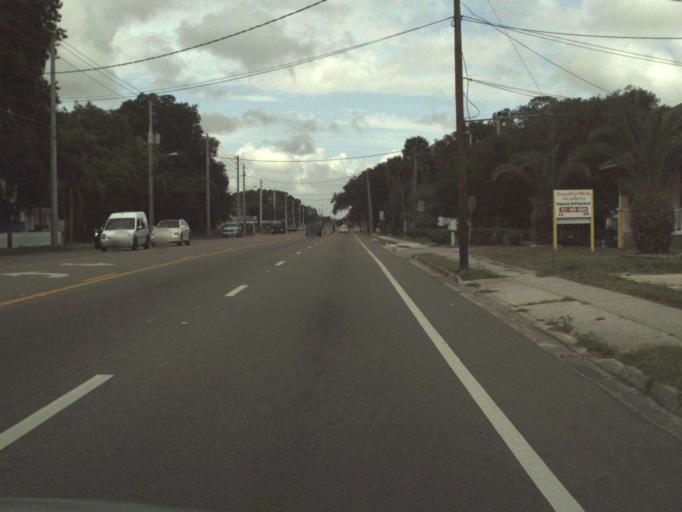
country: US
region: Florida
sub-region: Seminole County
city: Sanford
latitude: 28.8117
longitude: -81.2783
